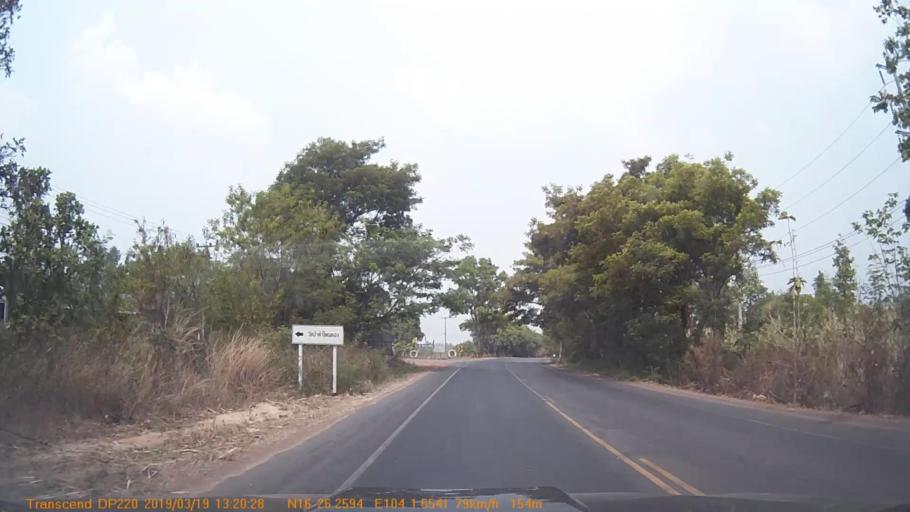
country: TH
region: Kalasin
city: Kuchinarai
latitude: 16.4379
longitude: 104.0260
